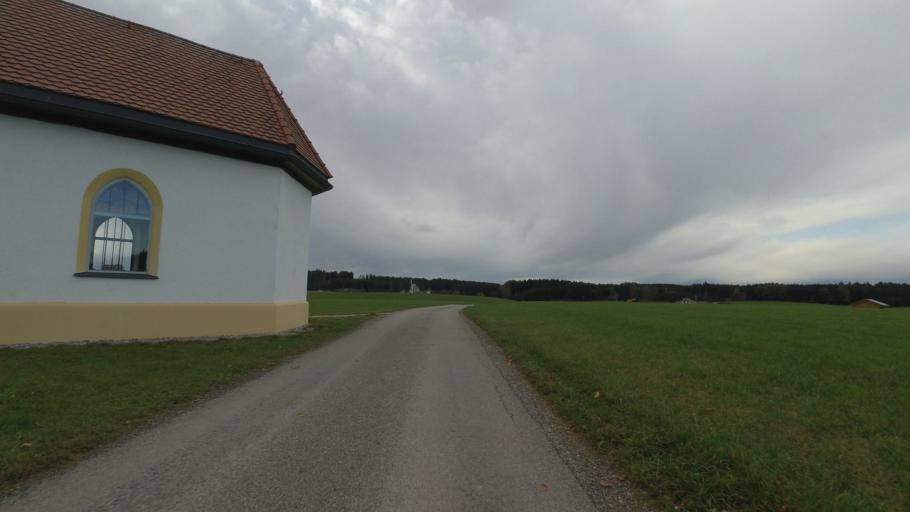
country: DE
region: Bavaria
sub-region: Upper Bavaria
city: Nussdorf
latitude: 47.9093
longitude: 12.5896
